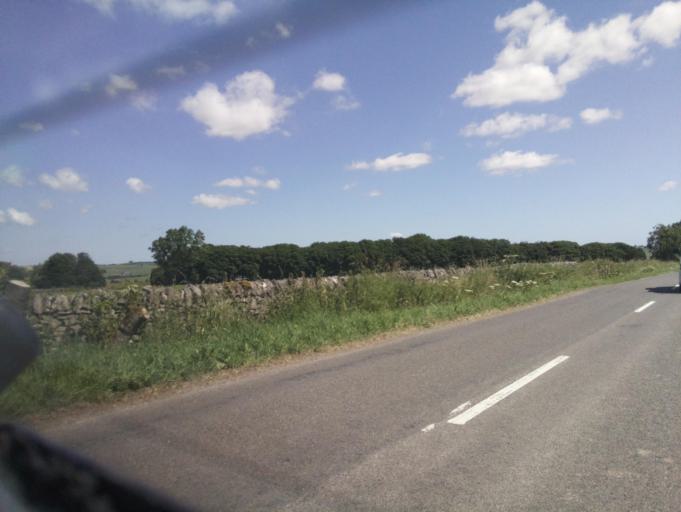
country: GB
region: England
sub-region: Derbyshire
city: Tideswell
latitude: 53.1915
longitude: -1.7974
